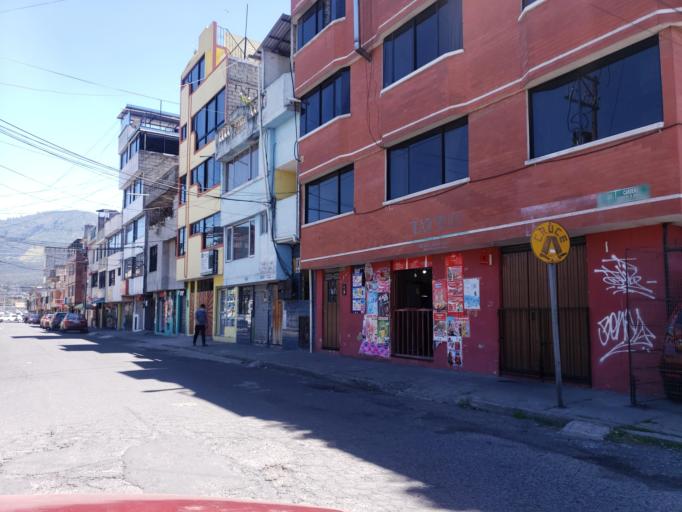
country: EC
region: Pichincha
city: Quito
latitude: -0.2686
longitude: -78.5355
